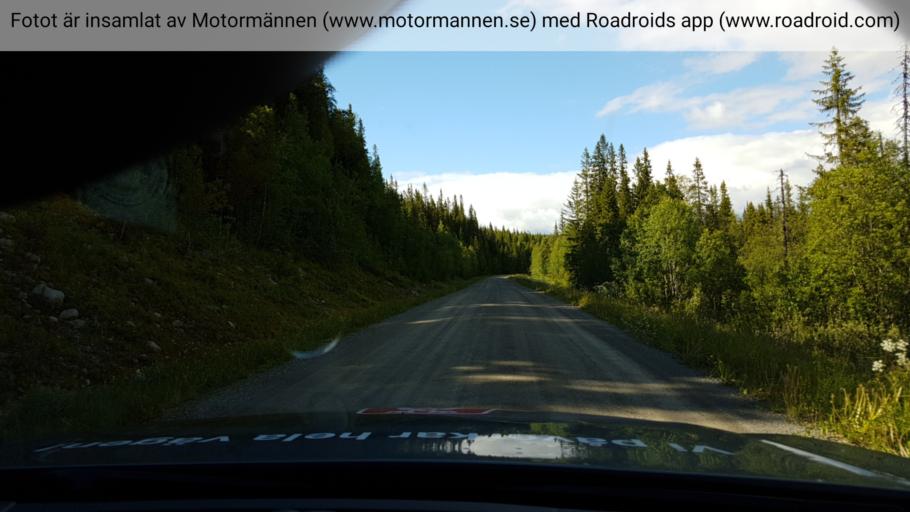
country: SE
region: Jaemtland
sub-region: Krokoms Kommun
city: Valla
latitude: 63.0421
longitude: 13.9625
